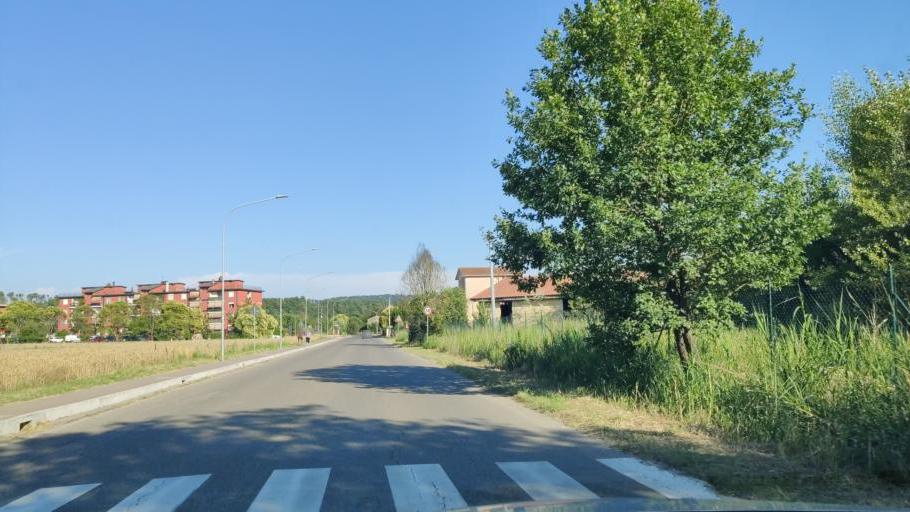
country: IT
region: Latium
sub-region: Provincia di Viterbo
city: Orte
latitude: 42.4670
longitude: 12.3916
